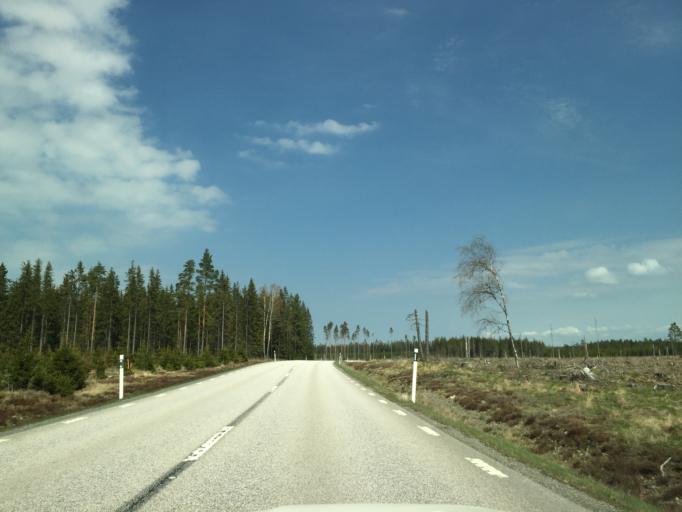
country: SE
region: Vaestra Goetaland
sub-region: Bengtsfors Kommun
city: Dals Langed
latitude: 58.8316
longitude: 12.1432
